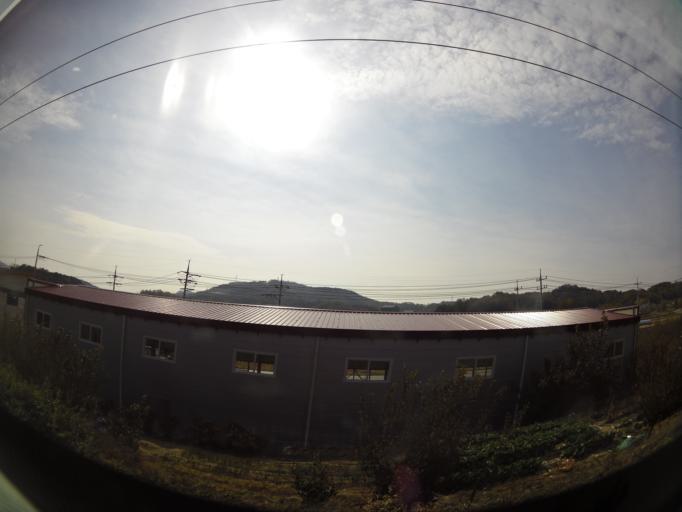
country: KR
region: Daejeon
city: Songgang-dong
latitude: 36.5363
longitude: 127.3470
